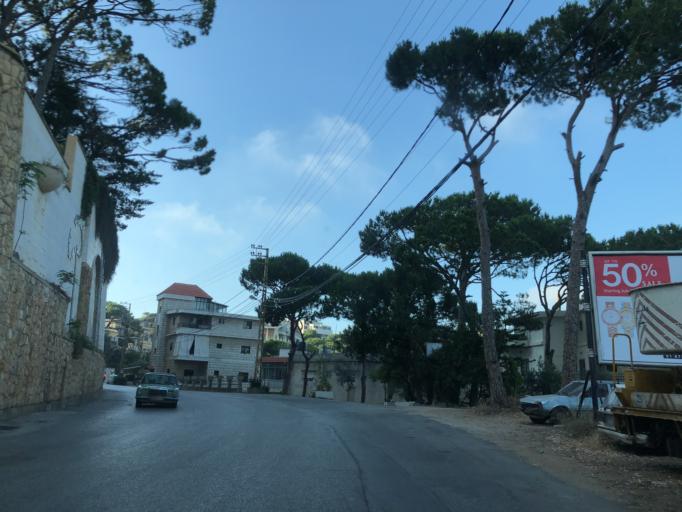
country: LB
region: Mont-Liban
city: Jdaidet el Matn
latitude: 33.8781
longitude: 35.6246
